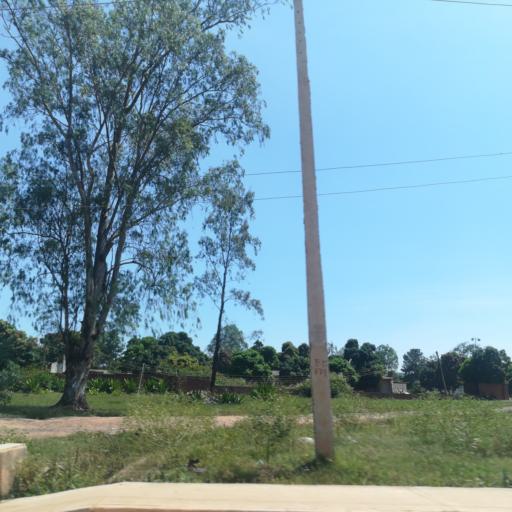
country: NG
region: Plateau
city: Bukuru
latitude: 9.8072
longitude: 8.8710
